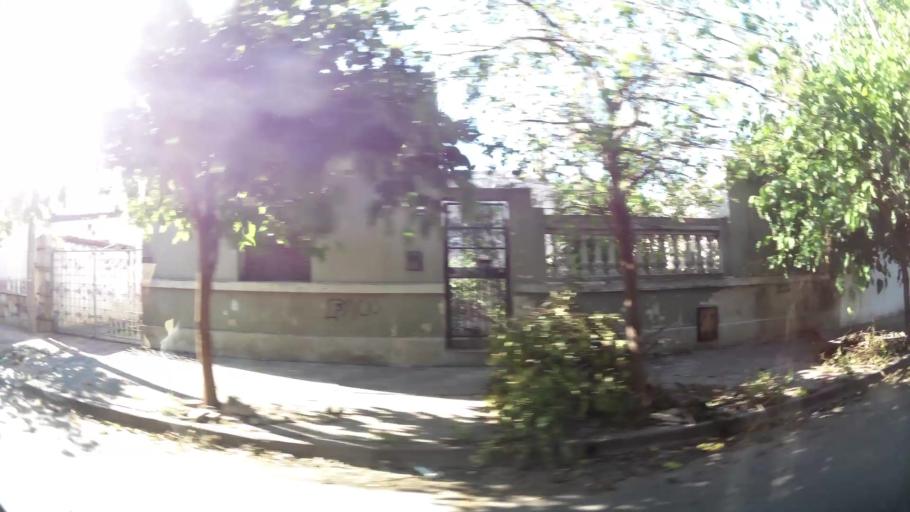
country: AR
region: Cordoba
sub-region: Departamento de Capital
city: Cordoba
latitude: -31.3998
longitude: -64.1588
